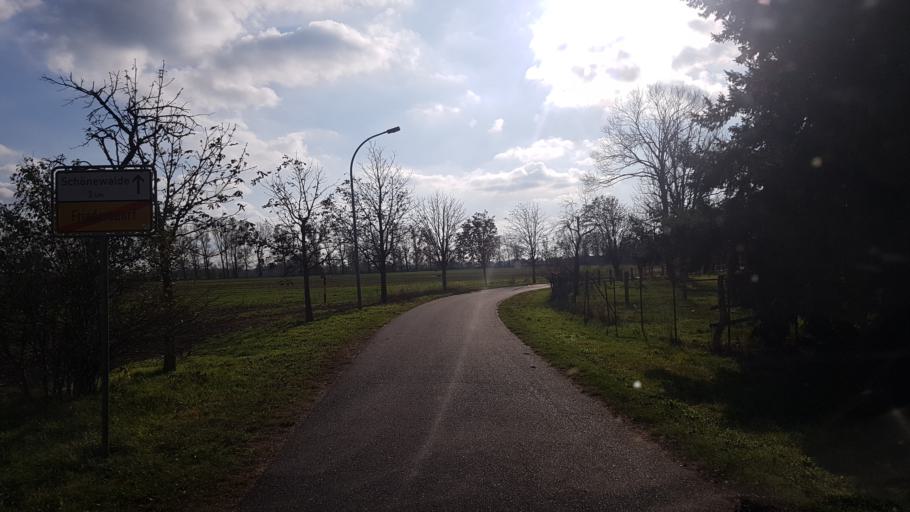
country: DE
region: Brandenburg
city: Schonewalde
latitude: 51.6979
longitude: 13.5737
